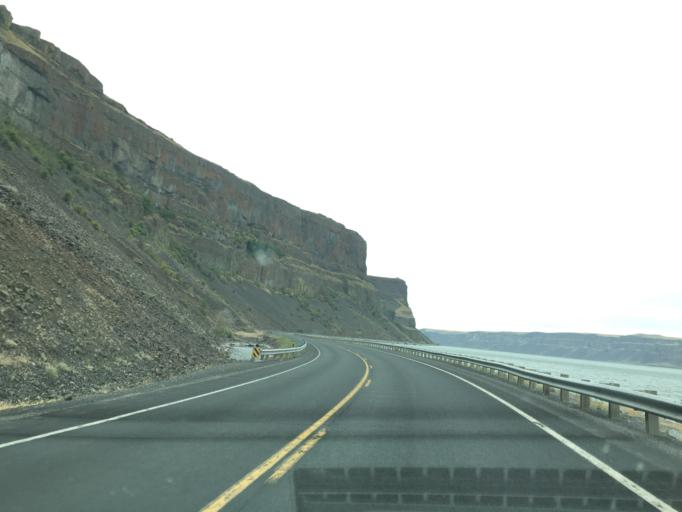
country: US
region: Washington
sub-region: Okanogan County
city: Coulee Dam
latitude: 47.8141
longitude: -119.1599
